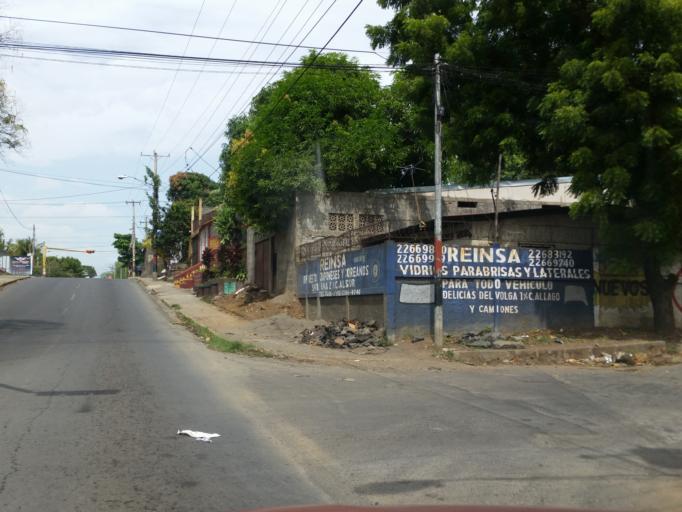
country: NI
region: Managua
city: Managua
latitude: 12.1074
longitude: -86.2986
